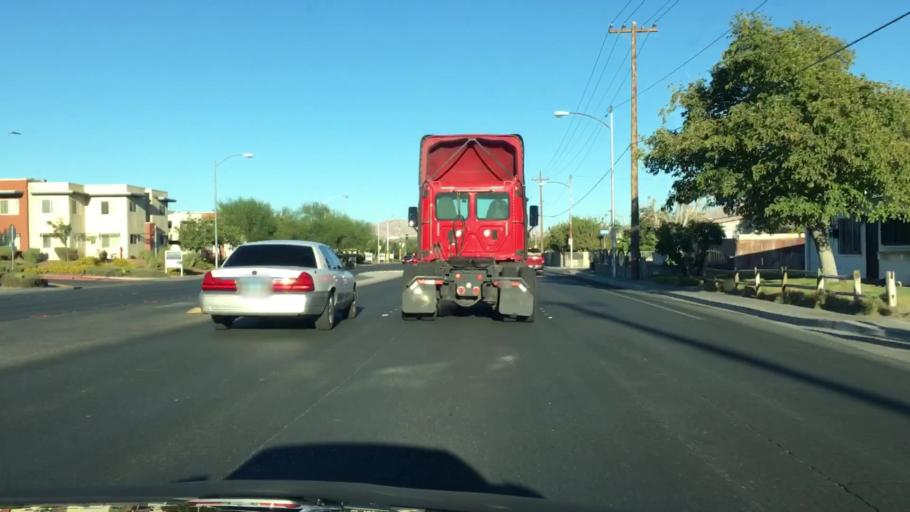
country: US
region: Nevada
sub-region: Clark County
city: North Las Vegas
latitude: 36.2176
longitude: -115.1154
